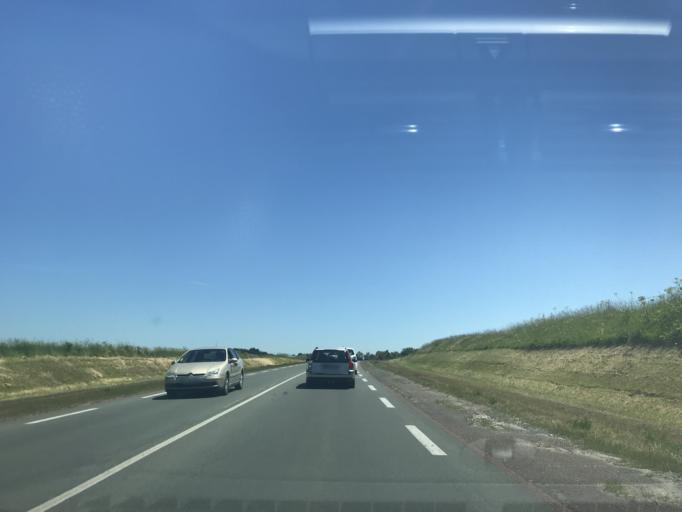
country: FR
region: Poitou-Charentes
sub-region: Departement de la Charente-Maritime
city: Saint-Georges-de-Didonne
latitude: 45.6111
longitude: -0.9794
